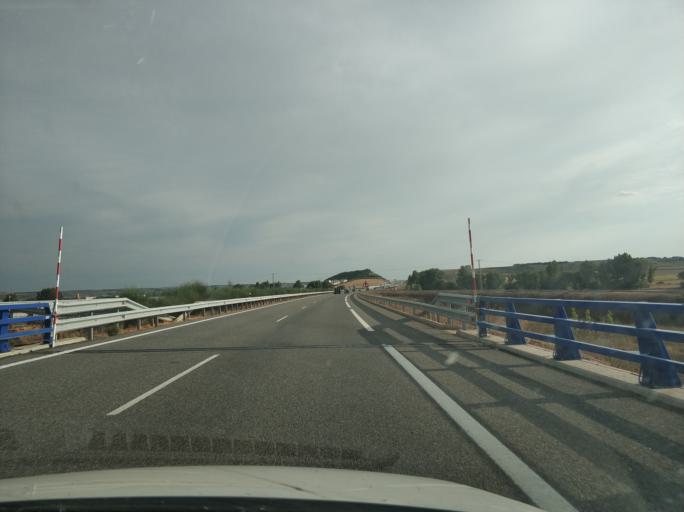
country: ES
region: Castille and Leon
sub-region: Provincia de Burgos
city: Quintanaortuno
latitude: 42.4632
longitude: -3.6880
